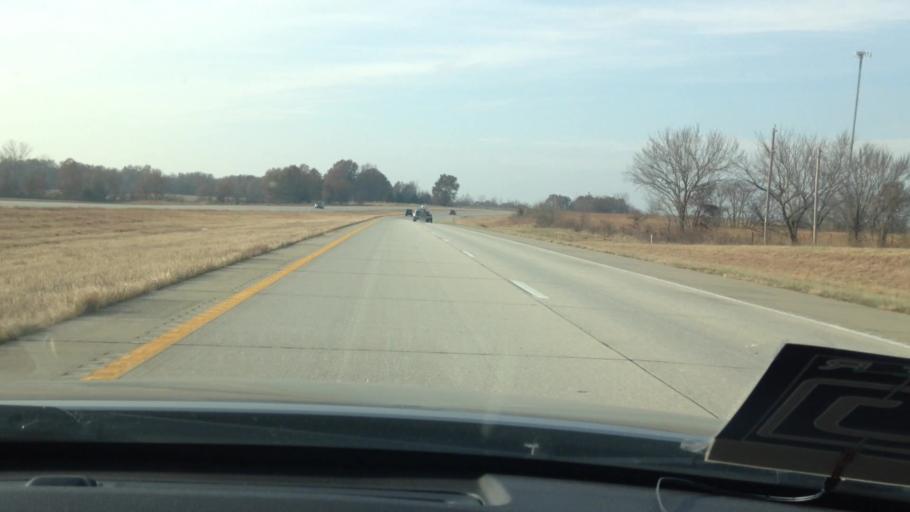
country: US
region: Missouri
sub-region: Henry County
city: Clinton
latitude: 38.4410
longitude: -93.9496
